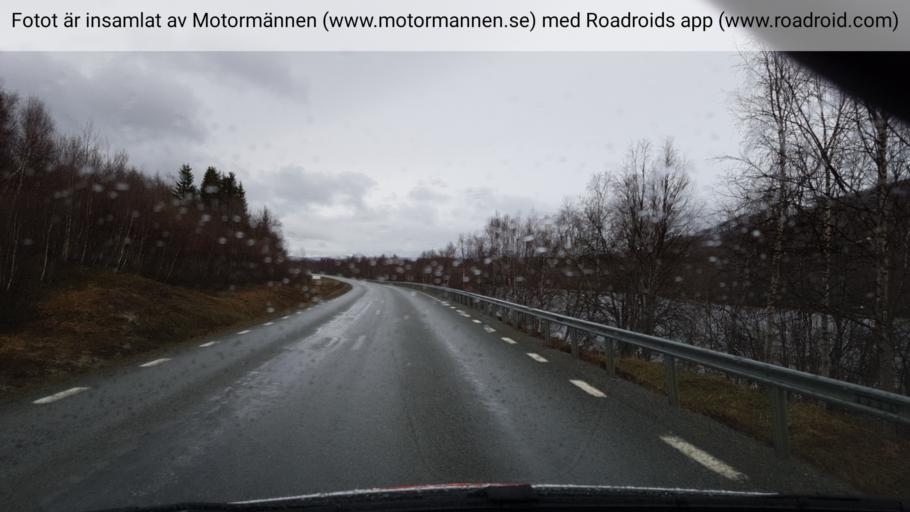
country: NO
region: Nordland
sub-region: Rana
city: Mo i Rana
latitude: 65.7881
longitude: 15.1051
